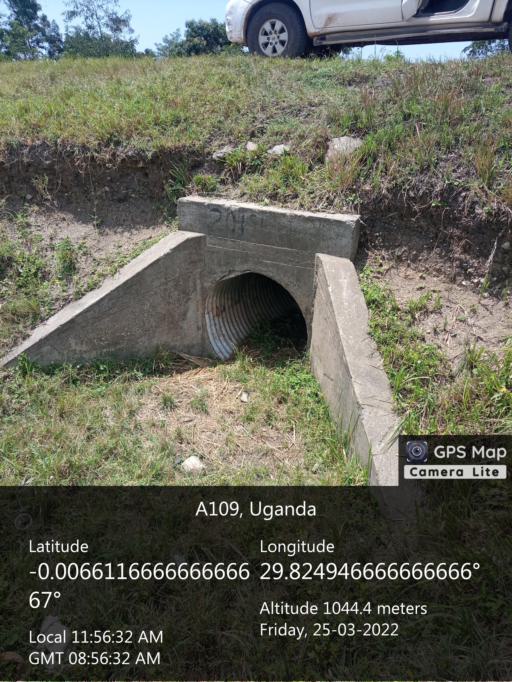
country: UG
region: Western Region
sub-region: Kasese District
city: Kilembe
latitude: -0.0067
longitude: 29.8250
